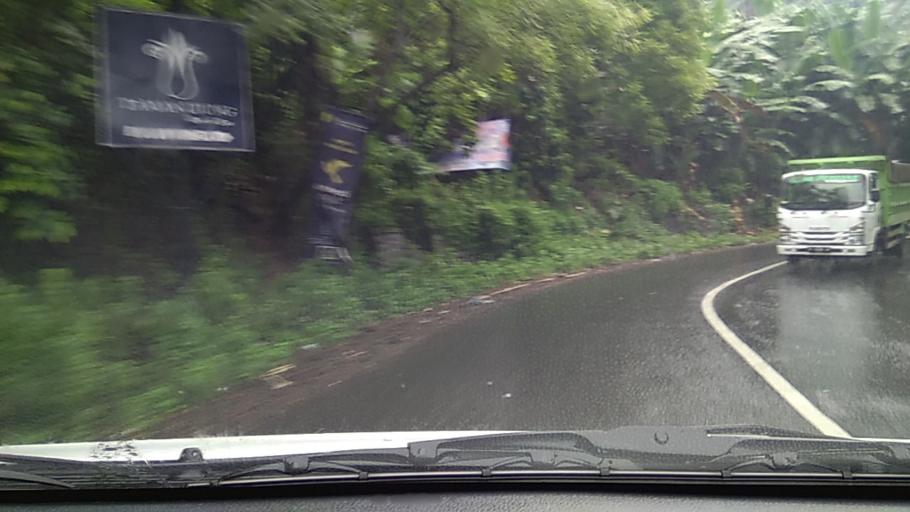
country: ID
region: Bali
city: Banjar Bugbug
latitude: -8.5003
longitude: 115.5823
